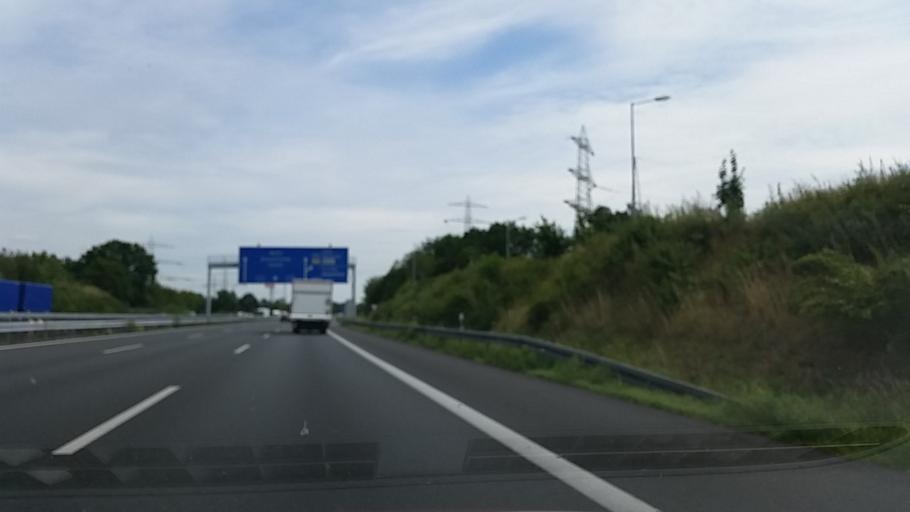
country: DE
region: Lower Saxony
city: Isernhagen Farster Bauerschaft
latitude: 52.4268
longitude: 9.8210
